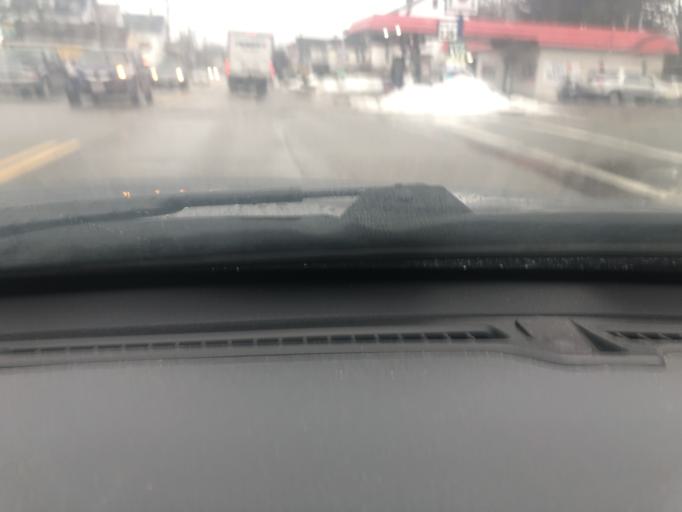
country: US
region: Massachusetts
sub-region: Plymouth County
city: Brockton
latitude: 42.1029
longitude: -71.0229
